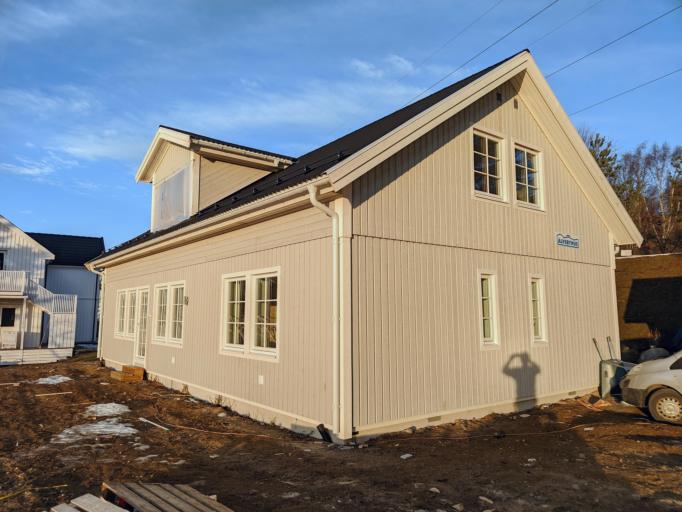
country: NO
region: Vestfold
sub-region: Svelvik
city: Svelvik
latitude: 59.6143
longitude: 10.4178
